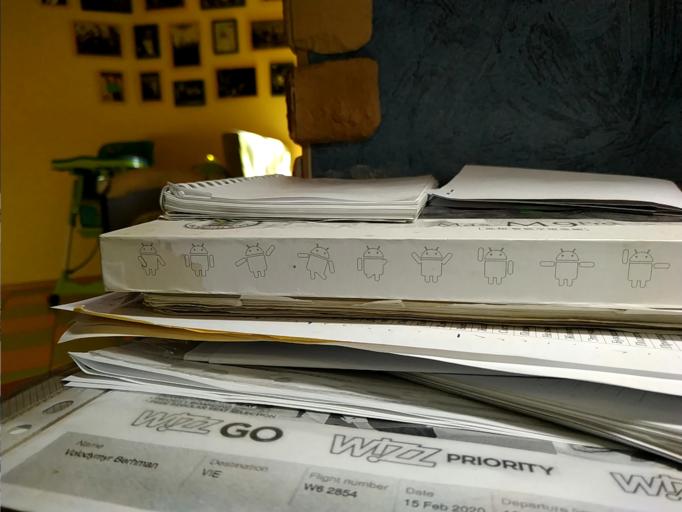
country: RU
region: Novgorod
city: Kholm
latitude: 57.2801
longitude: 31.2520
